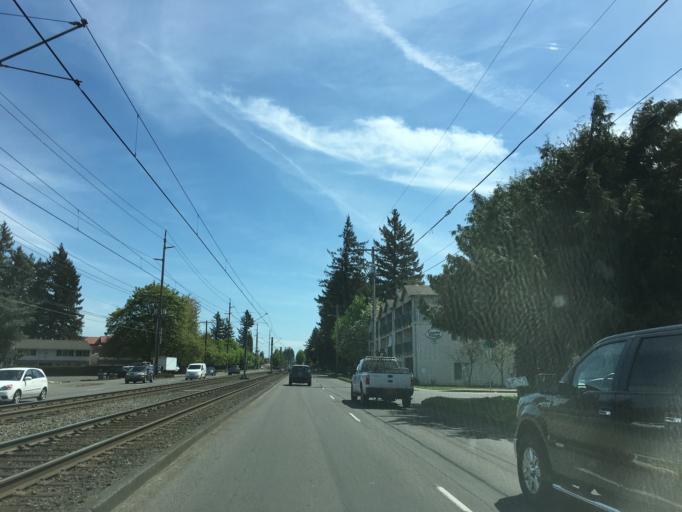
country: US
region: Oregon
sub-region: Multnomah County
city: Fairview
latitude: 45.5180
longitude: -122.4650
